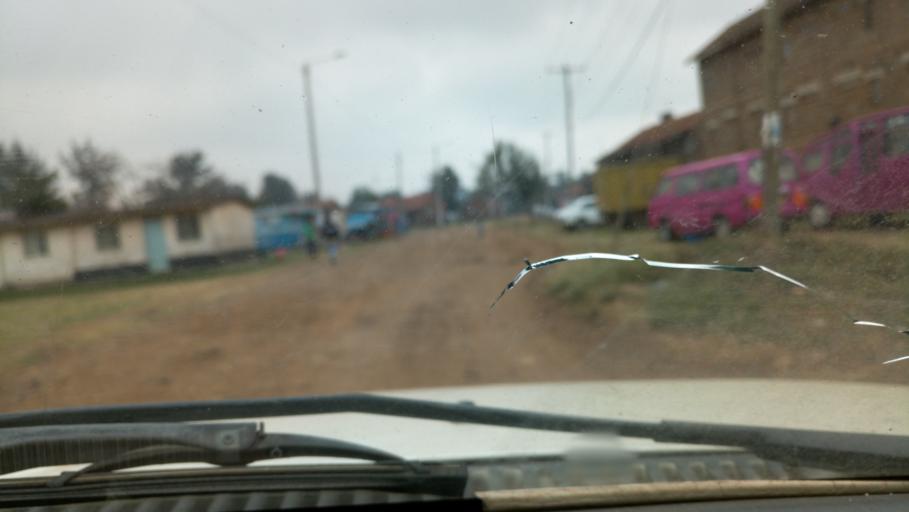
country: KE
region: Nairobi Area
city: Nairobi
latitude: -1.3029
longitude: 36.8033
